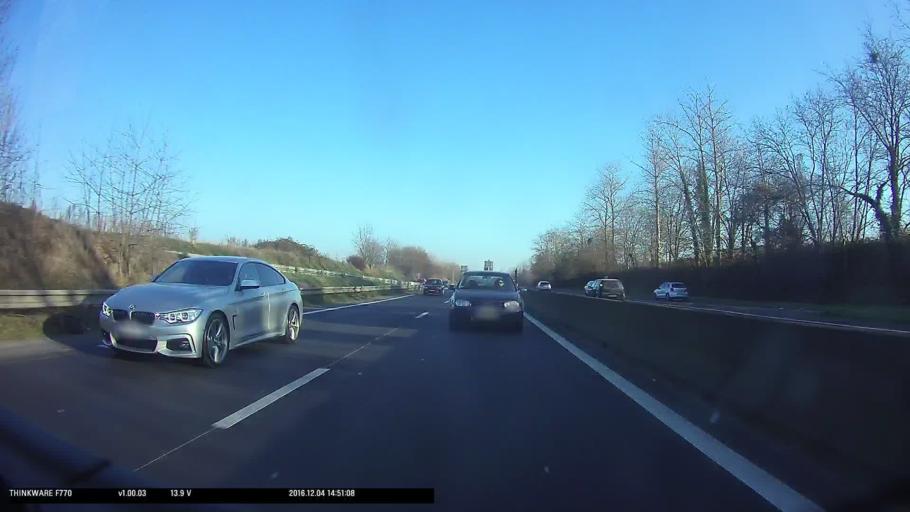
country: FR
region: Ile-de-France
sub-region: Departement du Val-d'Oise
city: Vaureal
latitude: 49.0585
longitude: 2.0326
